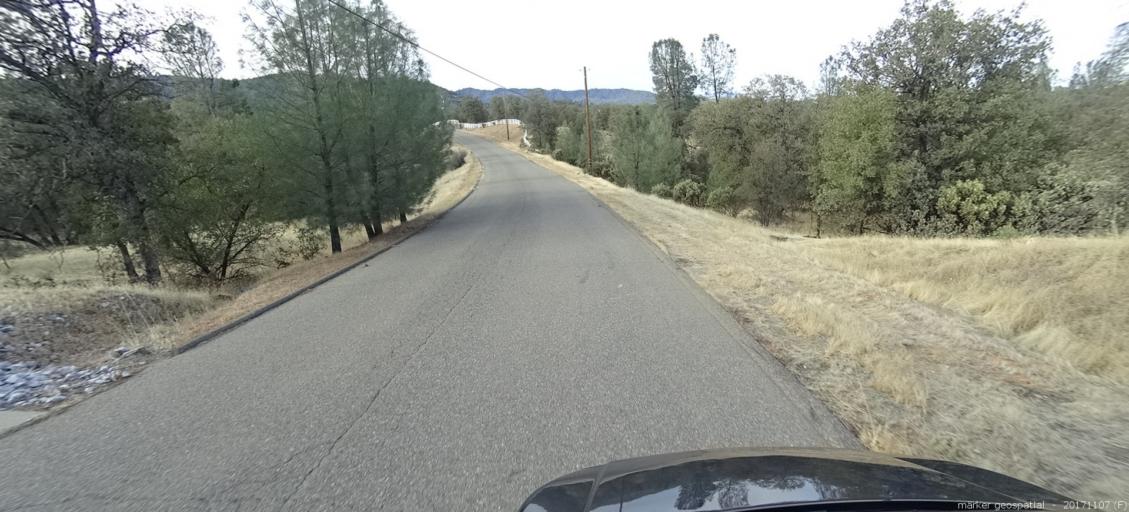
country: US
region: California
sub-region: Shasta County
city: Shasta
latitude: 40.5129
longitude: -122.4777
